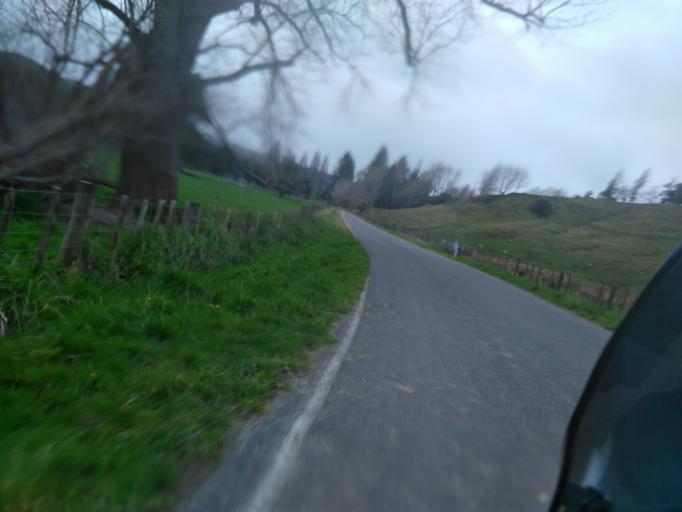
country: NZ
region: Gisborne
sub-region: Gisborne District
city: Gisborne
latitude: -38.6397
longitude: 177.6880
